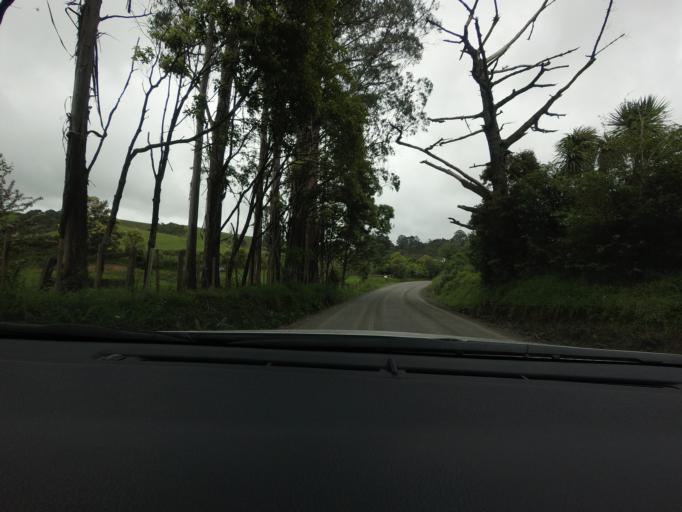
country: NZ
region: Auckland
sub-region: Auckland
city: Warkworth
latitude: -36.4805
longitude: 174.5581
